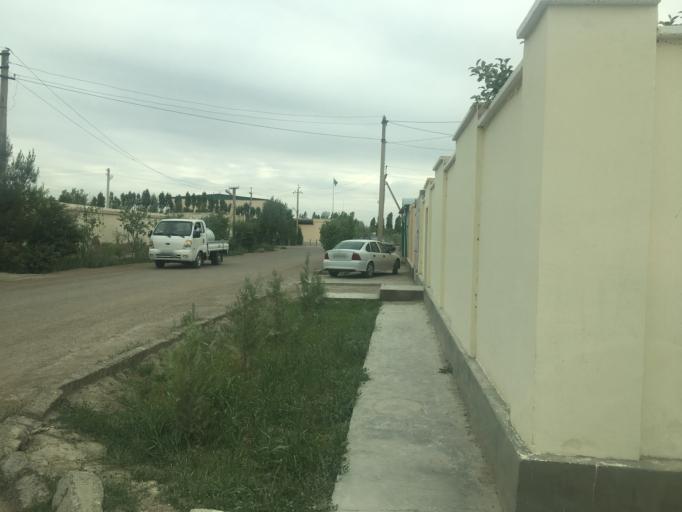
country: TM
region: Dasoguz
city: Dasoguz
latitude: 41.8368
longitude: 59.9344
